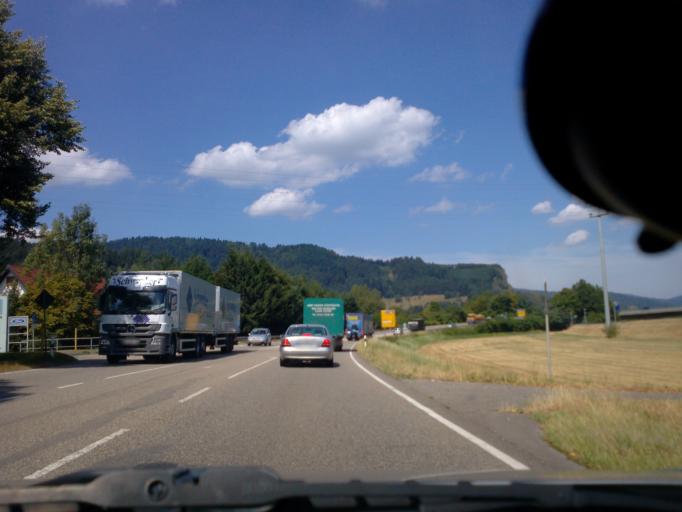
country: DE
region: Baden-Wuerttemberg
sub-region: Freiburg Region
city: Steinach
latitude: 48.2826
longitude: 8.0768
